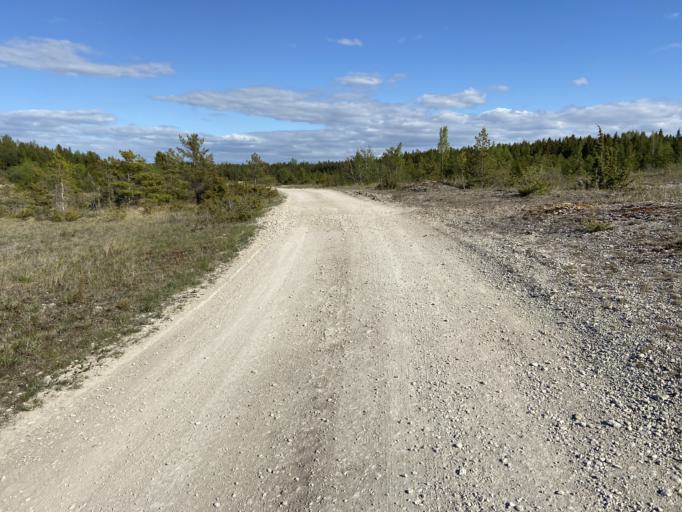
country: EE
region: Harju
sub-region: Paldiski linn
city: Paldiski
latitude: 59.2686
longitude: 23.7392
